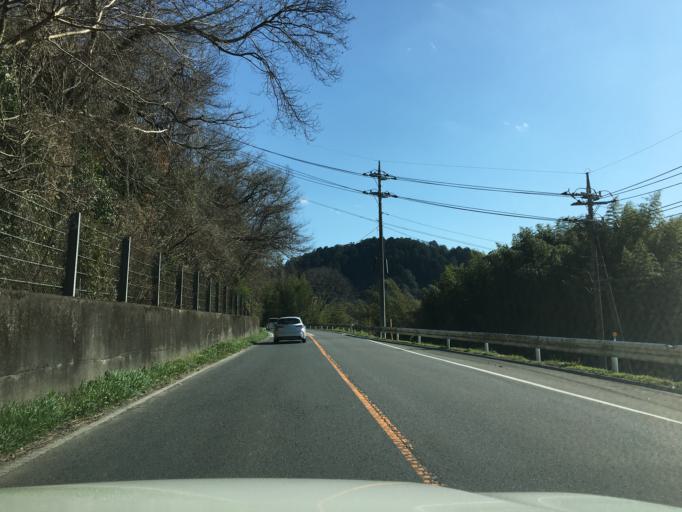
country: JP
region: Ibaraki
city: Omiya
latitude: 36.5541
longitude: 140.3221
